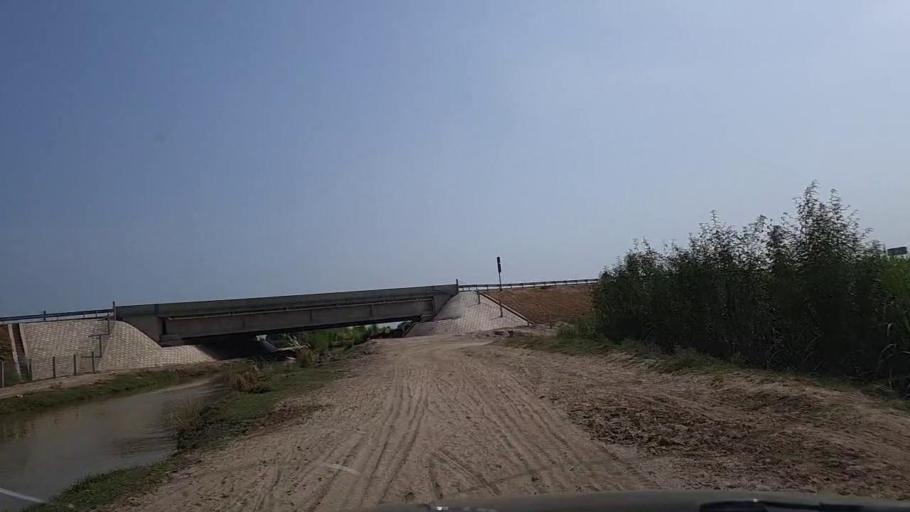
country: PK
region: Sindh
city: Ghotki
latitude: 28.0636
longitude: 69.3825
